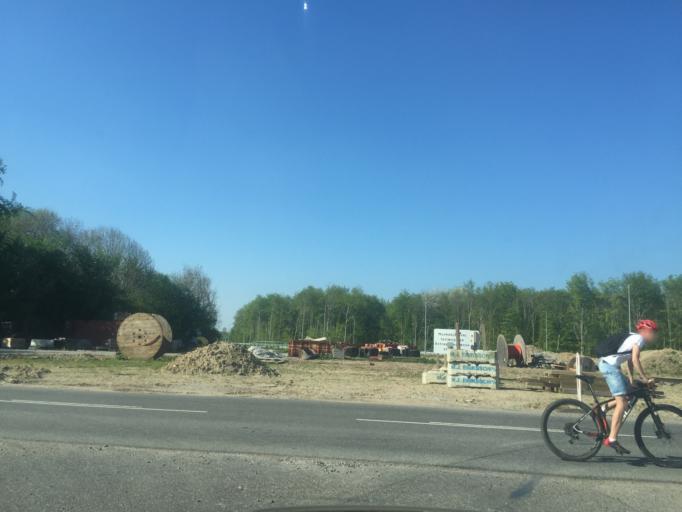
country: DK
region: South Denmark
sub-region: Odense Kommune
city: Hojby
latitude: 55.3567
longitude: 10.4158
